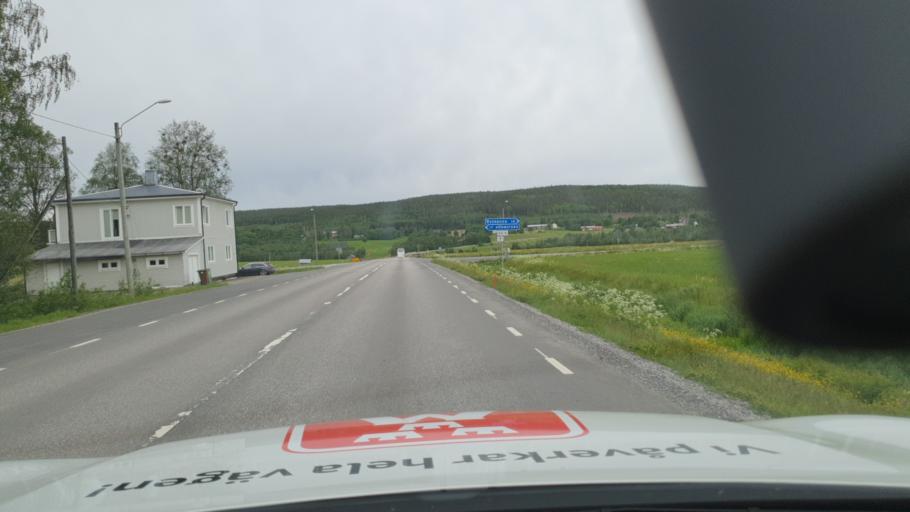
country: SE
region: Vaesterbotten
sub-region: Vannas Kommun
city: Vannasby
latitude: 63.7785
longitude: 19.8690
